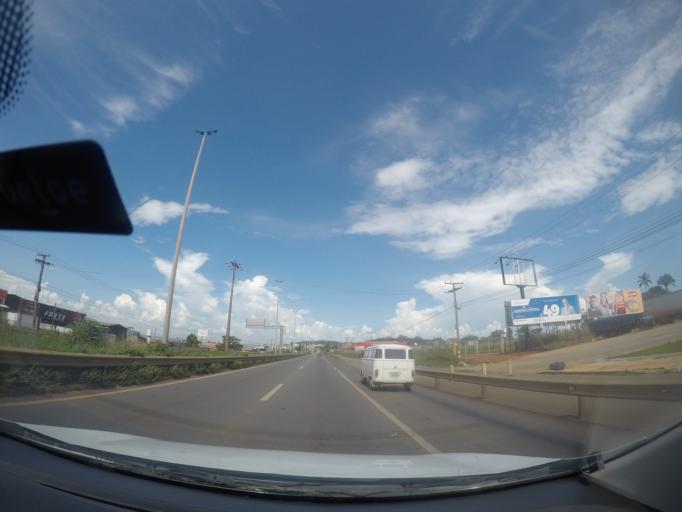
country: BR
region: Goias
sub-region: Trindade
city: Trindade
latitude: -16.6576
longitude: -49.3755
